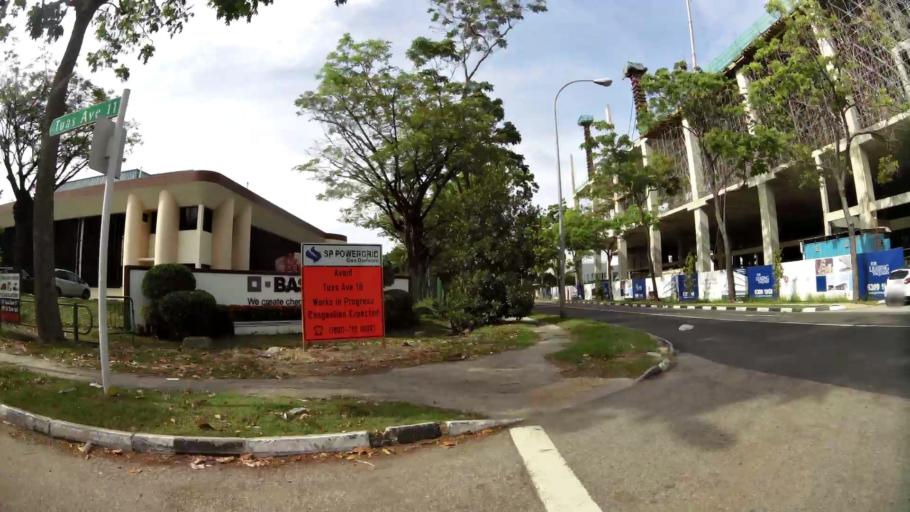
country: MY
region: Johor
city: Johor Bahru
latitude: 1.3277
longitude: 103.6390
